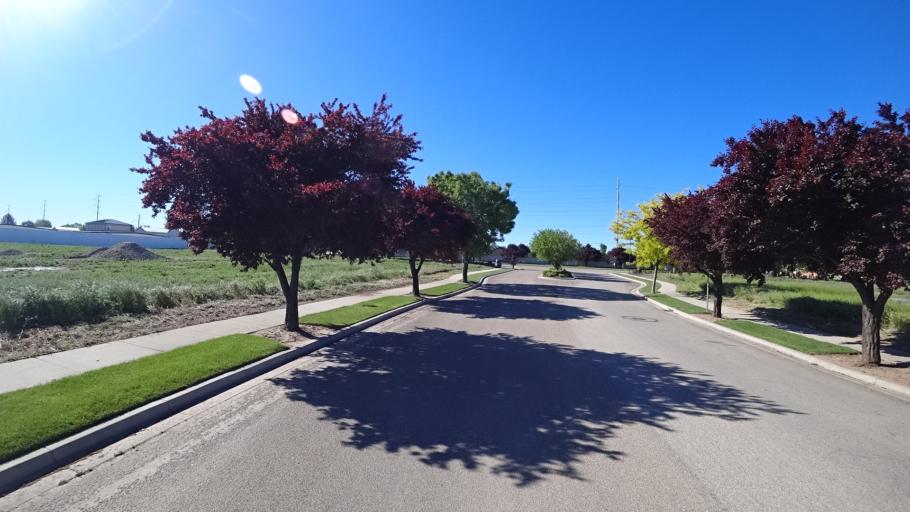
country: US
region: Idaho
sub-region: Ada County
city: Meridian
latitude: 43.6492
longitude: -116.4296
